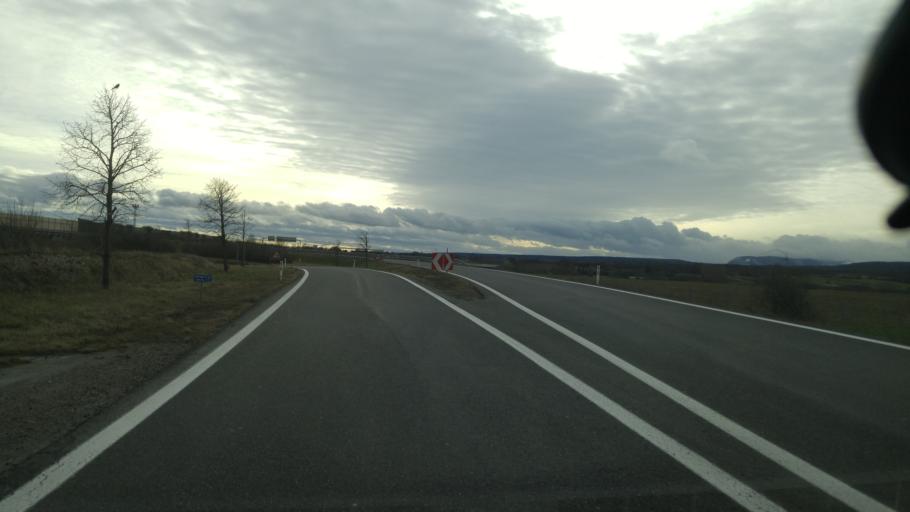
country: AT
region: Lower Austria
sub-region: Politischer Bezirk Baden
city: Kottingbrunn
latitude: 47.9536
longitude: 16.2179
